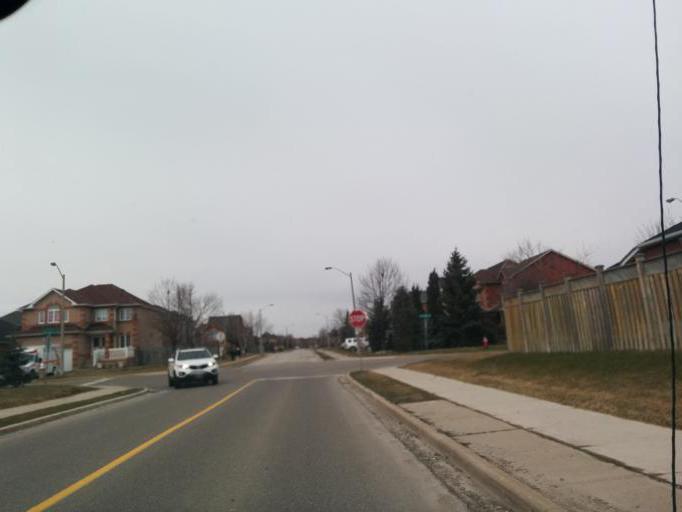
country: CA
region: Ontario
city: Brampton
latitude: 43.7258
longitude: -79.8193
